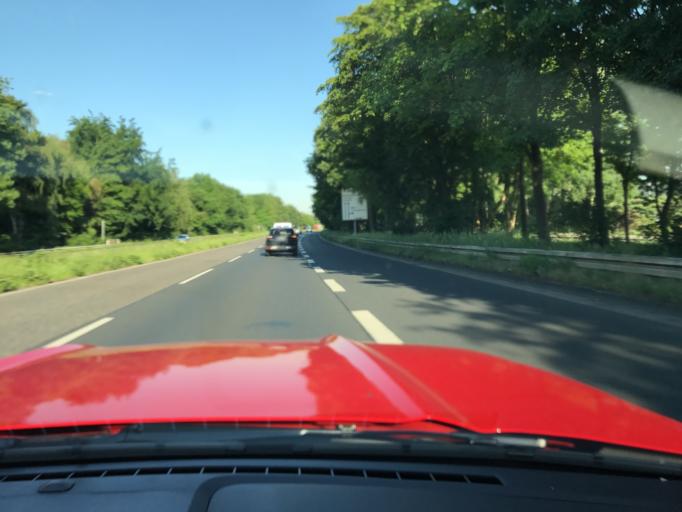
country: DE
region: North Rhine-Westphalia
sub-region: Regierungsbezirk Koln
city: Leverkusen
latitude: 51.0259
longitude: 6.9333
